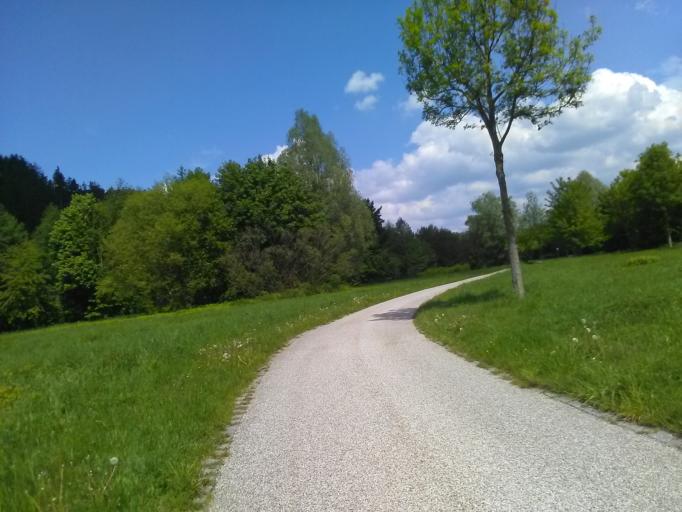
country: DE
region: Bavaria
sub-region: Upper Franconia
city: Kronach
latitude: 50.2233
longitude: 11.3150
